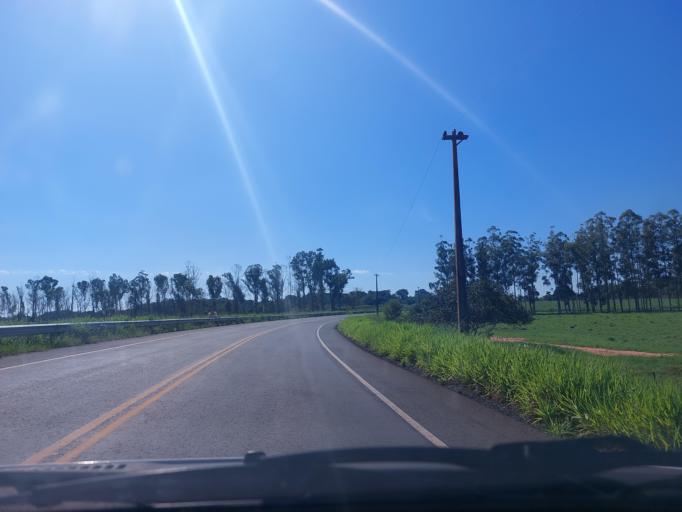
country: PY
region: San Pedro
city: Guayaybi
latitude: -24.3182
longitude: -56.1810
